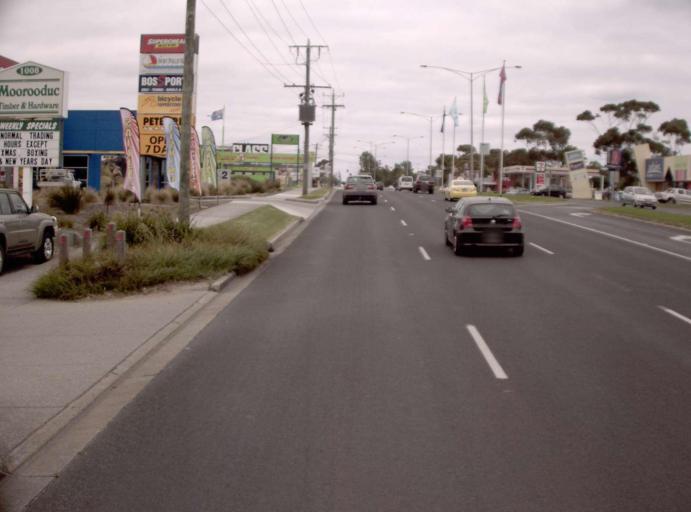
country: AU
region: Victoria
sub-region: Mornington Peninsula
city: Mornington
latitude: -38.2272
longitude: 145.0479
